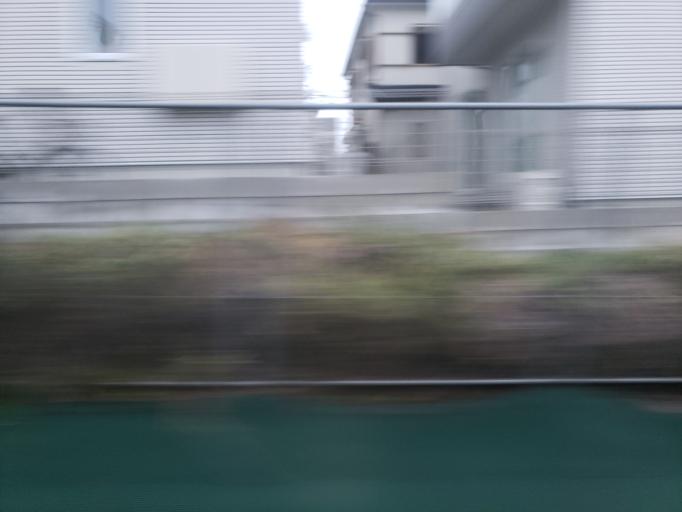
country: JP
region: Hyogo
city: Akashi
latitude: 34.6759
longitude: 134.9474
